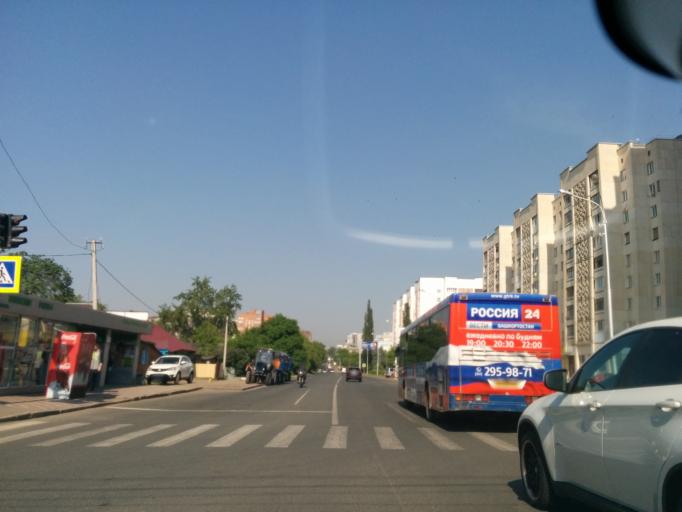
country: RU
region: Bashkortostan
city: Ufa
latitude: 54.7257
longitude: 55.9665
